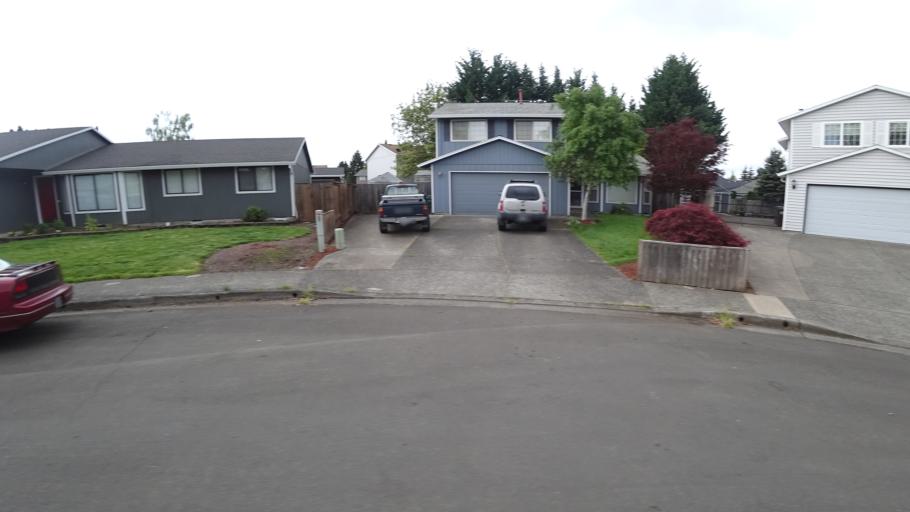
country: US
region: Oregon
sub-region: Washington County
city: Hillsboro
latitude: 45.5395
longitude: -122.9769
